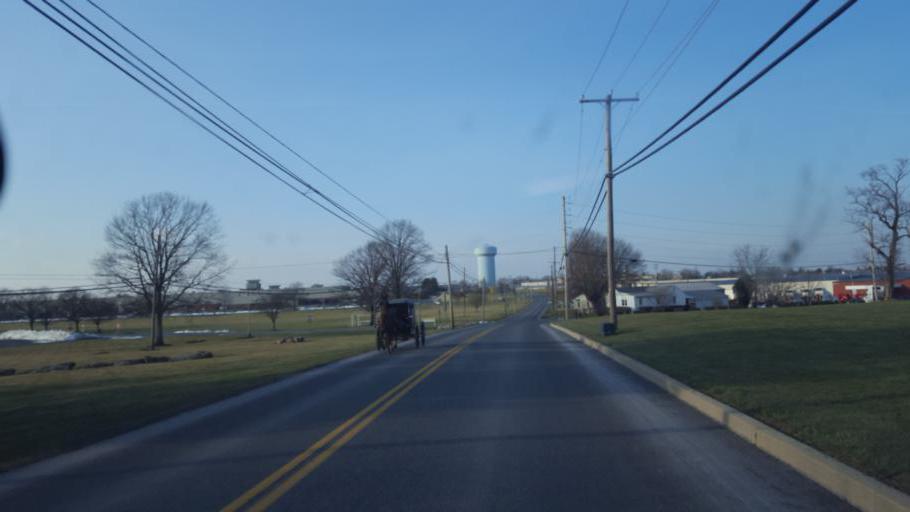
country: US
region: Pennsylvania
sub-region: Lancaster County
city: New Holland
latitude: 40.0889
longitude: -76.0989
